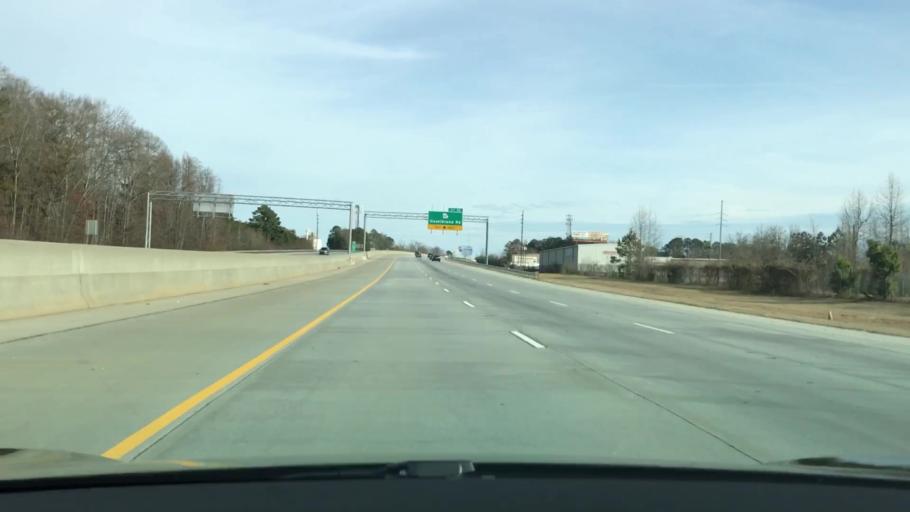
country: US
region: Georgia
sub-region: Newton County
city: Covington
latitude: 33.6152
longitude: -83.8401
